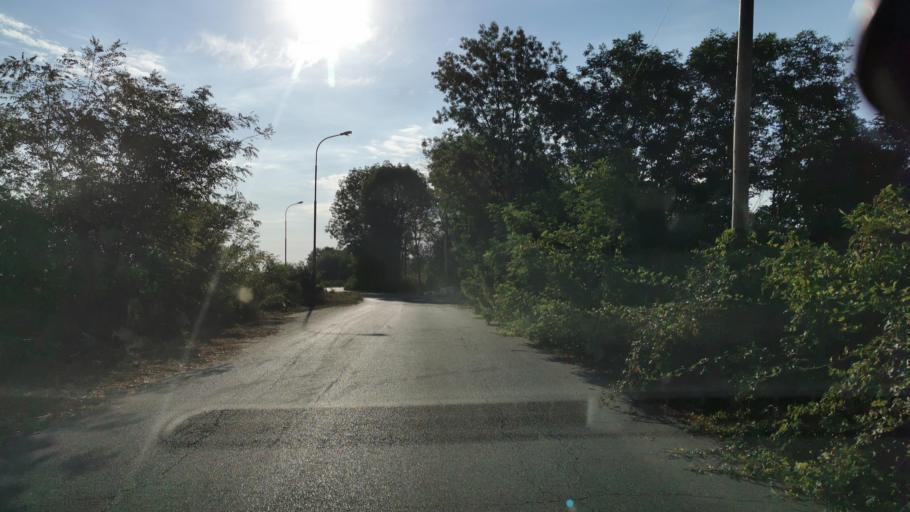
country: IT
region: Piedmont
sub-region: Provincia di Torino
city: Volpiano
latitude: 45.1751
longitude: 7.7756
